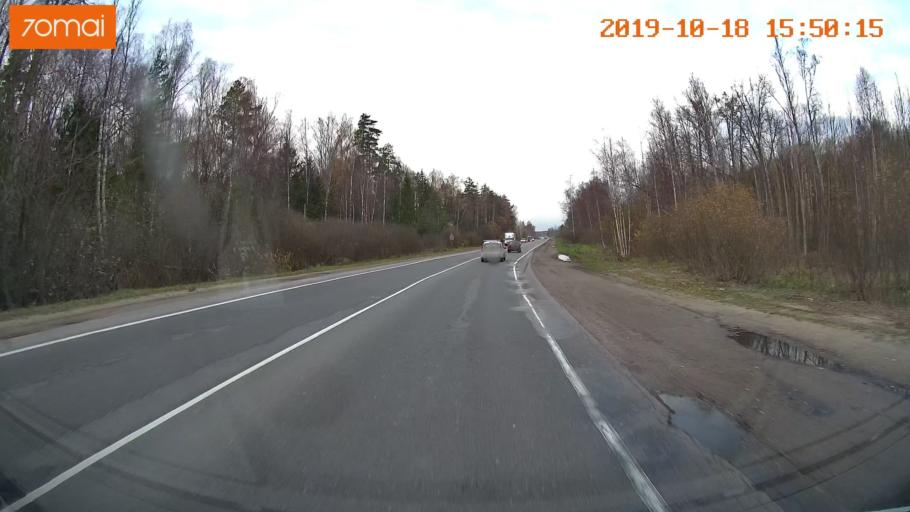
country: RU
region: Vladimir
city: Kommunar
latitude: 56.0307
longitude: 40.5622
